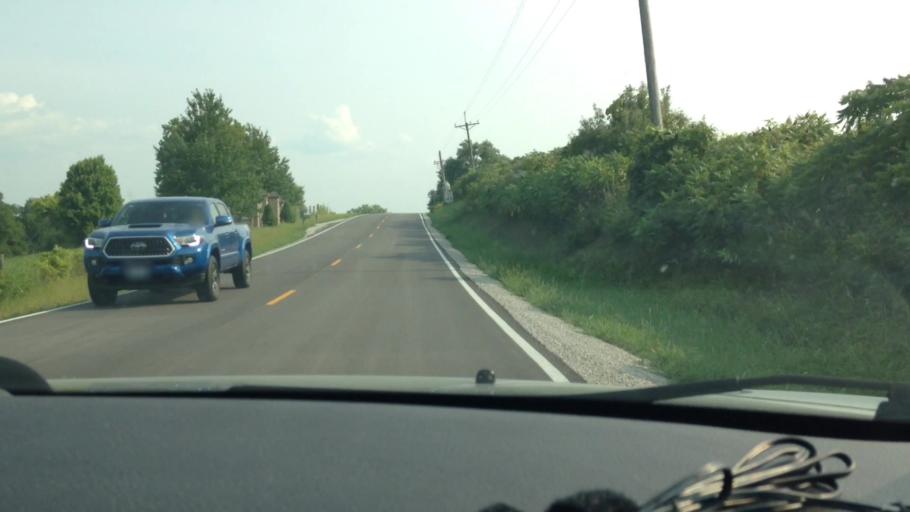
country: US
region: Missouri
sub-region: Platte County
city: Platte City
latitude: 39.4005
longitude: -94.7797
